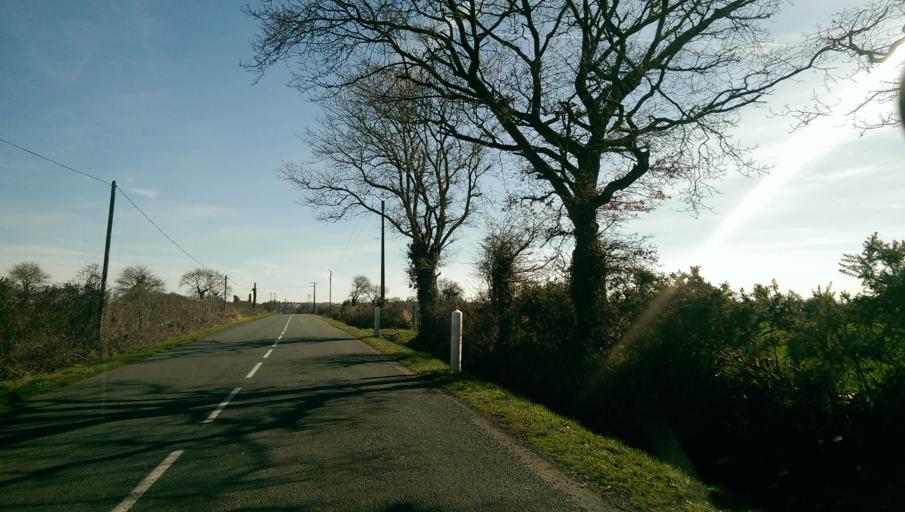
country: FR
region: Pays de la Loire
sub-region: Departement de la Vendee
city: Beaurepaire
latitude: 46.9316
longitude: -1.0983
